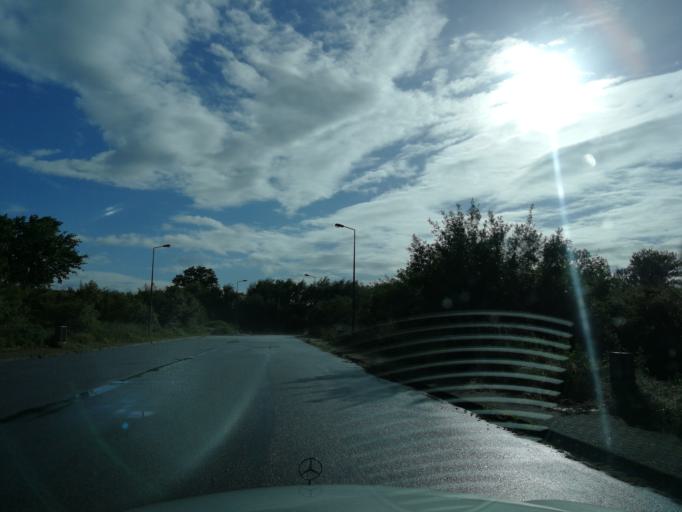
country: PT
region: Braga
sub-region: Braga
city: Braga
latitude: 41.5680
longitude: -8.4493
